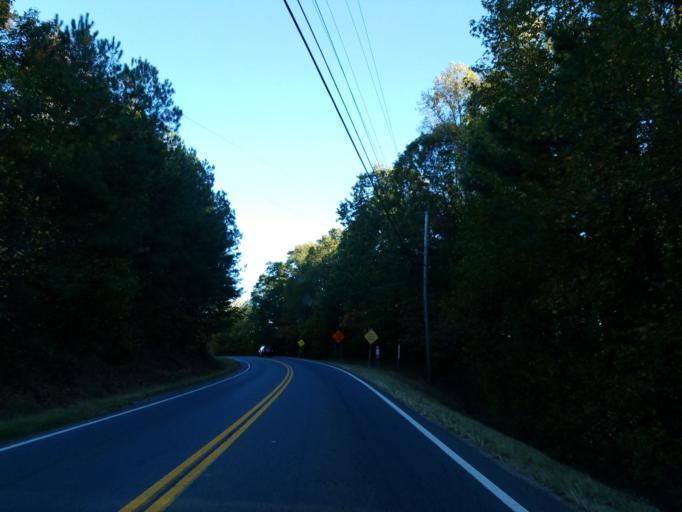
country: US
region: Georgia
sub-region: Dawson County
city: Dawsonville
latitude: 34.3748
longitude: -84.0456
